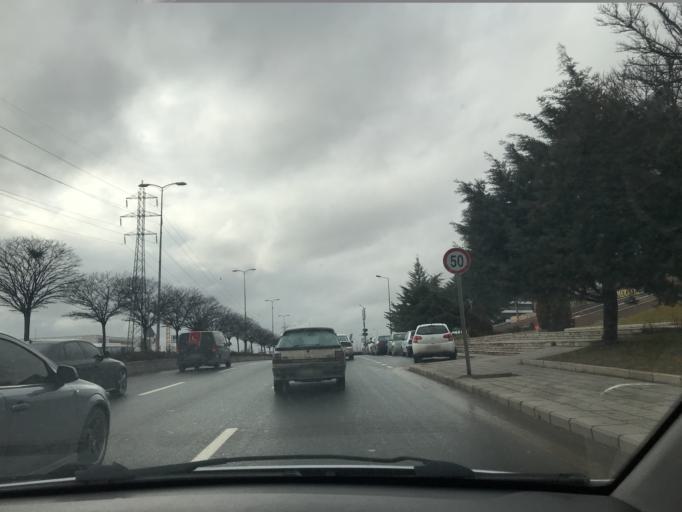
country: TR
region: Ankara
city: Batikent
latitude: 39.9602
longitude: 32.7793
